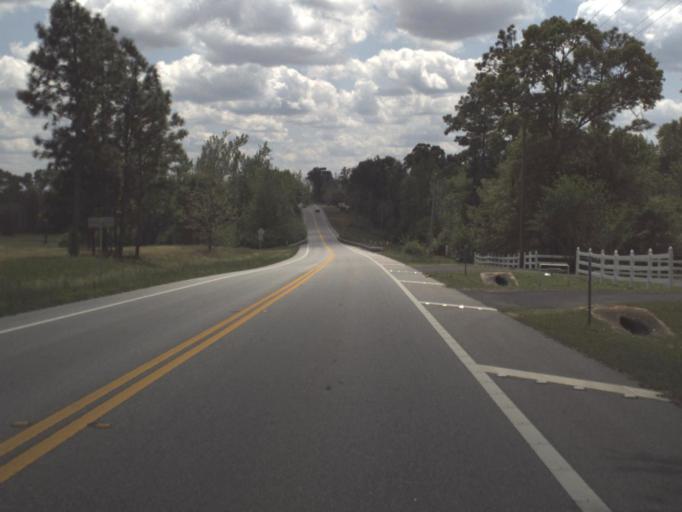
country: US
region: Alabama
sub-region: Escambia County
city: Atmore
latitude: 30.9515
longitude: -87.4870
